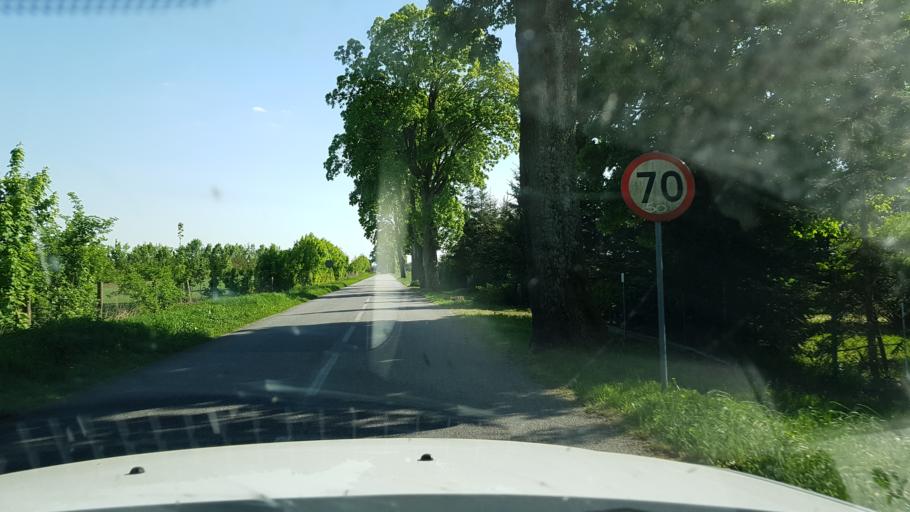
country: PL
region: West Pomeranian Voivodeship
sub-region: Powiat lobeski
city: Resko
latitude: 53.7909
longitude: 15.4114
